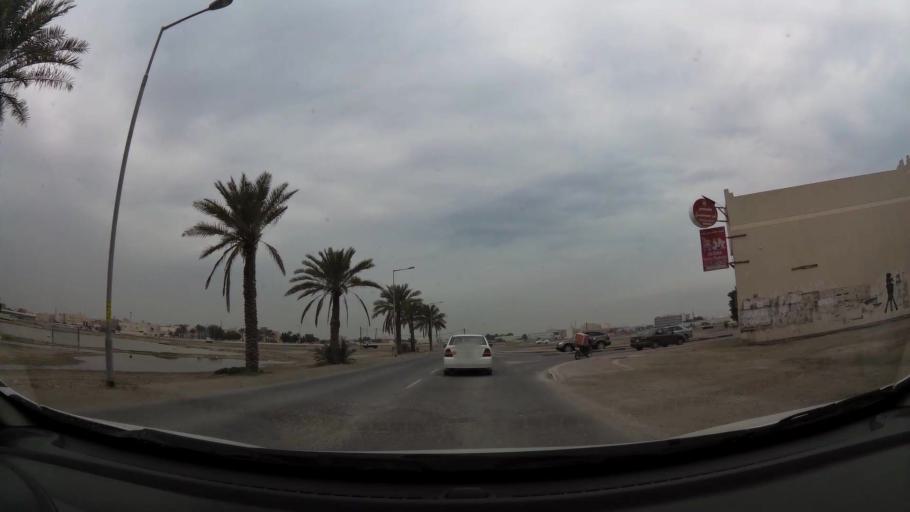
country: BH
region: Northern
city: Sitrah
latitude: 26.1696
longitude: 50.6202
